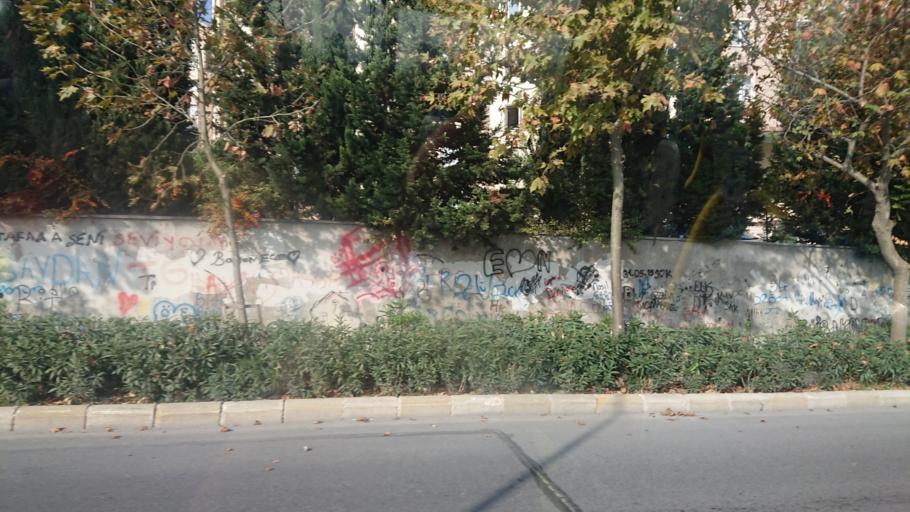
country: TR
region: Istanbul
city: Esenyurt
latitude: 41.0751
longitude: 28.6685
